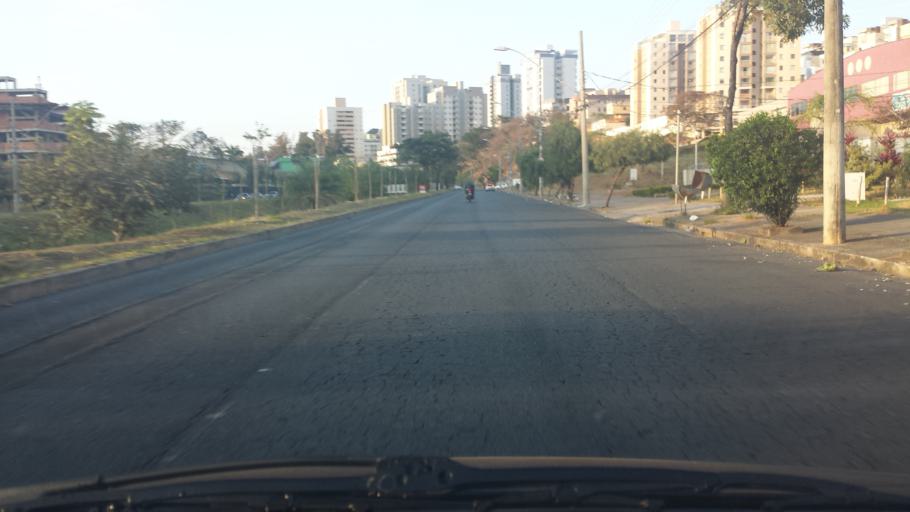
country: BR
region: Minas Gerais
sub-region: Belo Horizonte
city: Belo Horizonte
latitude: -19.8842
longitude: -43.9937
